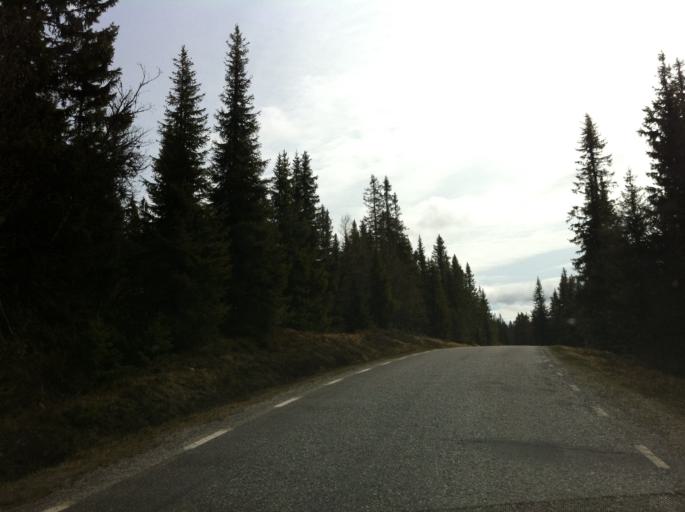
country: NO
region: Hedmark
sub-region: Engerdal
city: Engerdal
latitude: 62.3040
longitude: 12.8007
